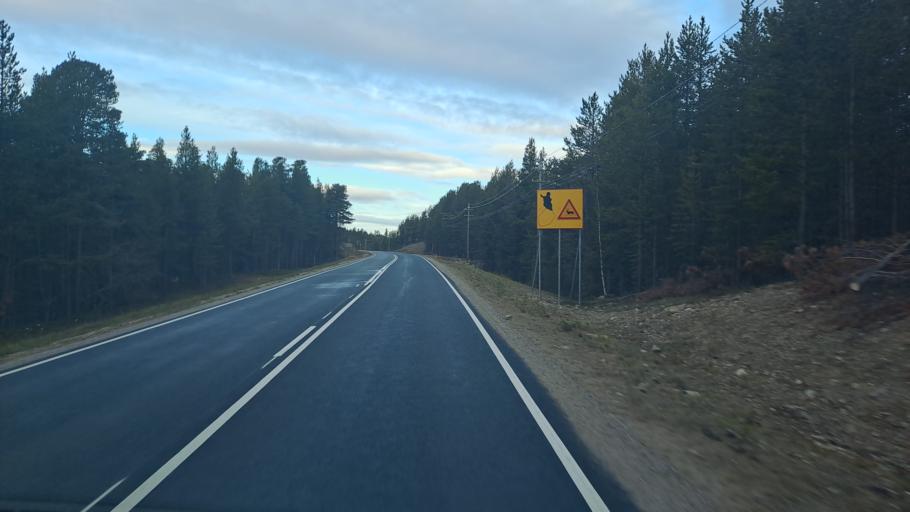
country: FI
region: Lapland
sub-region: Pohjois-Lappi
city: Inari
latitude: 68.9128
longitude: 27.0038
